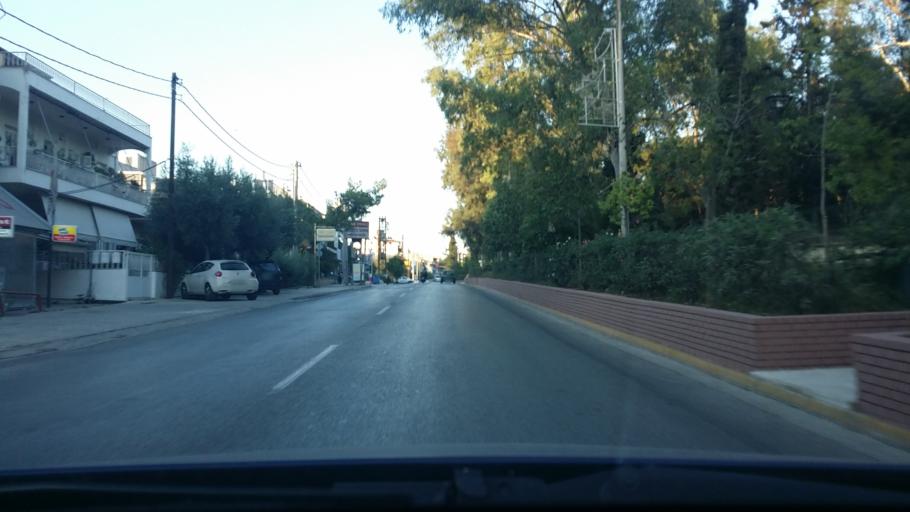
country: GR
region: Attica
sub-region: Nomarchia Athinas
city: Nea Filadelfeia
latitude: 38.0453
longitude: 23.7444
